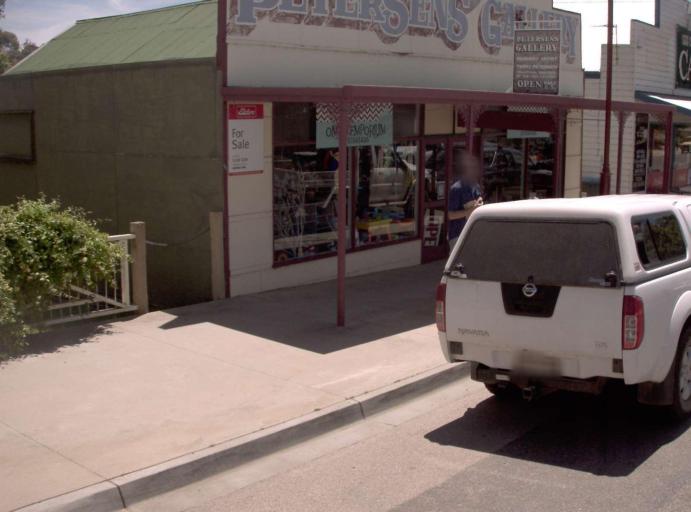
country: AU
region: Victoria
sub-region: Alpine
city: Mount Beauty
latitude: -37.1006
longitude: 147.5914
